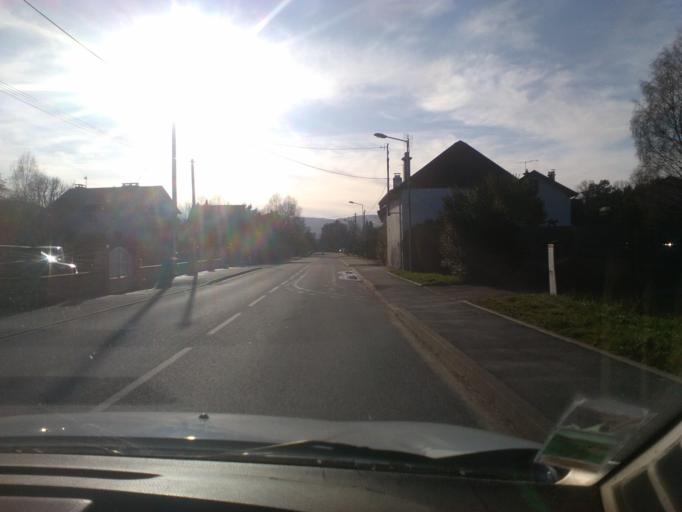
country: FR
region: Lorraine
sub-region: Departement des Vosges
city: Saint-Ame
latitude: 48.0187
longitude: 6.6542
